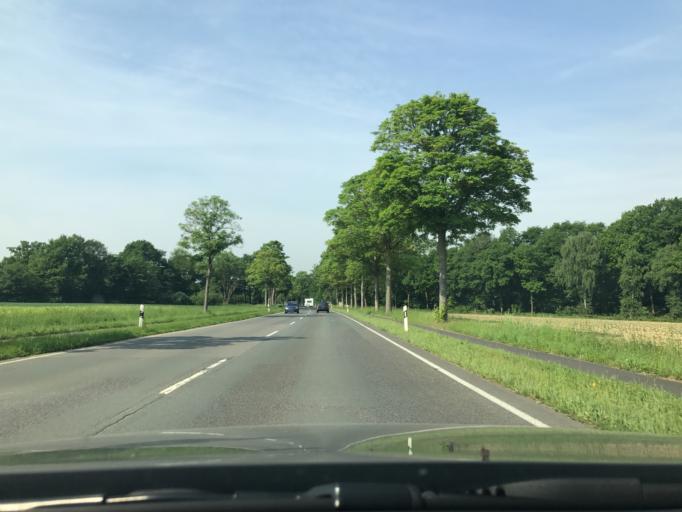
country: DE
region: North Rhine-Westphalia
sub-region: Regierungsbezirk Dusseldorf
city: Wachtendonk
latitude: 51.4306
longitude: 6.3784
